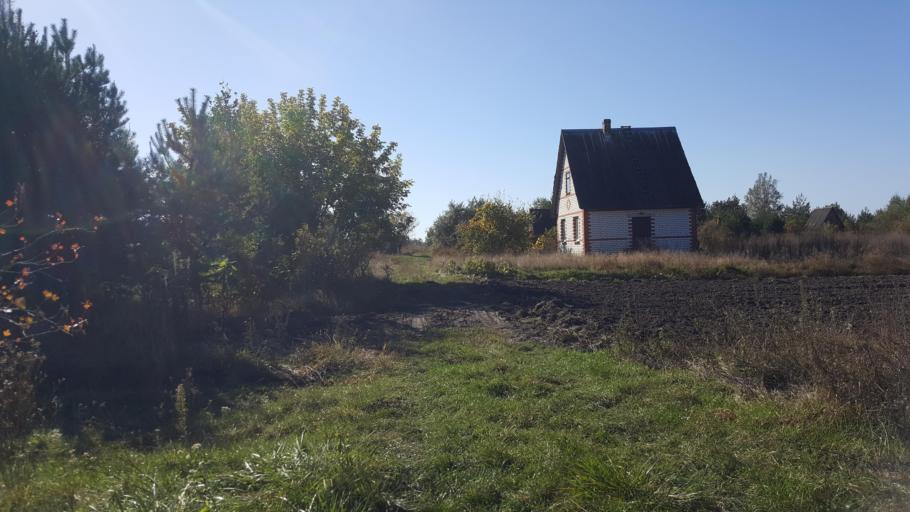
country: BY
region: Brest
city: Kamyanyets
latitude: 52.4342
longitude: 23.8842
